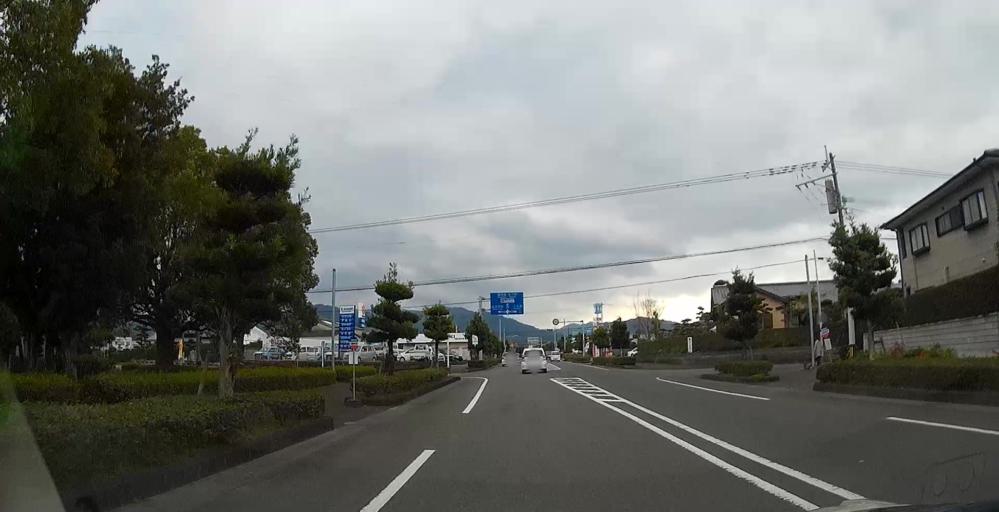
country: JP
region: Kagoshima
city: Izumi
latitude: 32.0834
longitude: 130.3443
